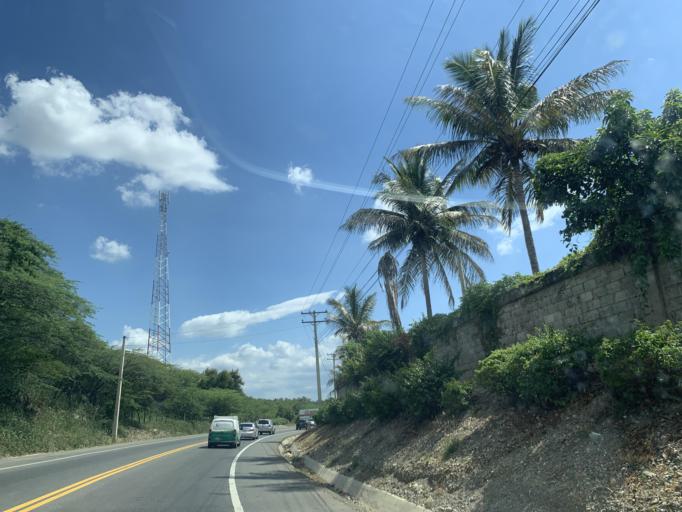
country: DO
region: Santiago
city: Villa Bisono
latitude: 19.5813
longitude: -70.8452
